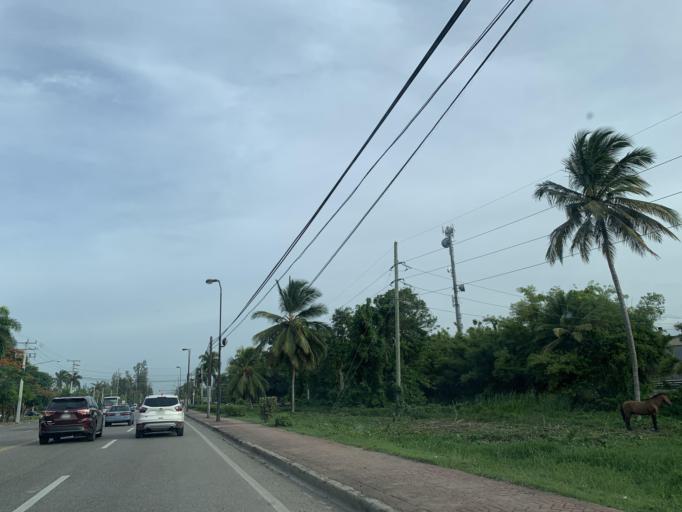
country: DO
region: Puerto Plata
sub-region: Puerto Plata
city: Puerto Plata
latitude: 19.7686
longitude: -70.6522
